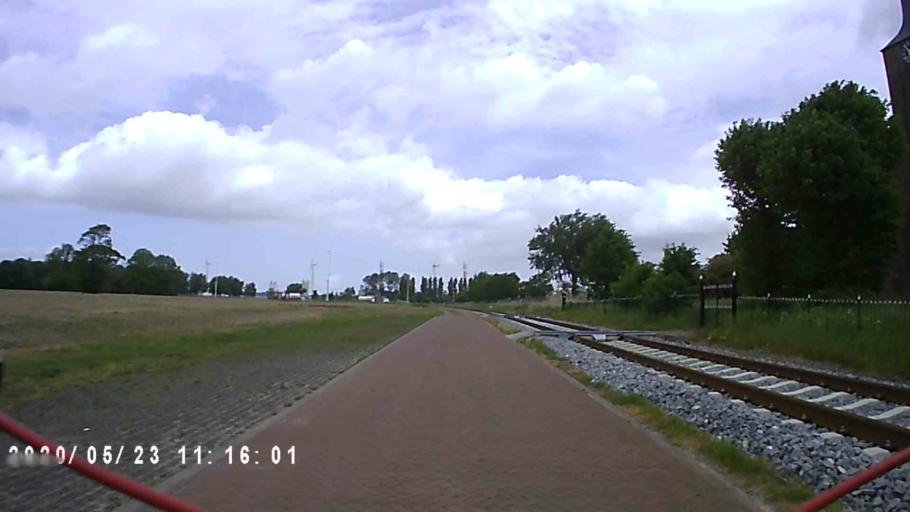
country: NL
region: Groningen
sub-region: Gemeente Delfzijl
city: Delfzijl
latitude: 53.3087
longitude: 6.9648
